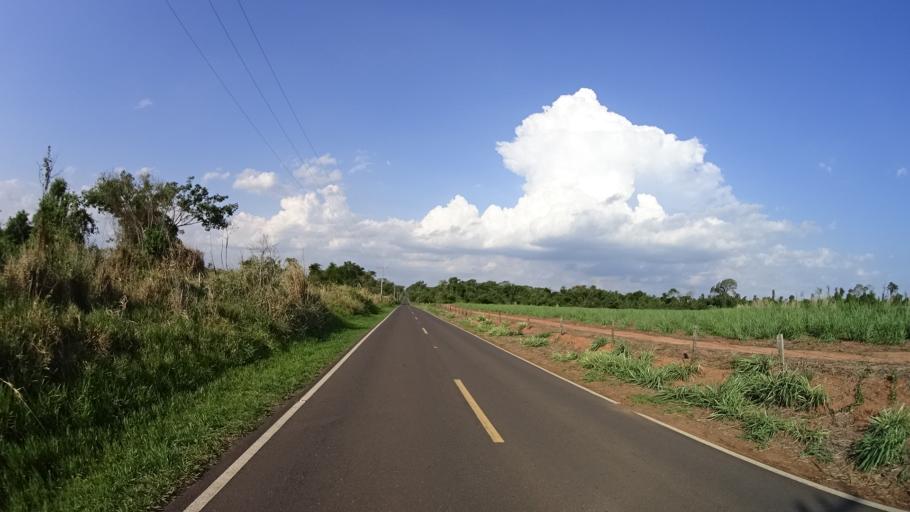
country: BR
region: Sao Paulo
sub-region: Urupes
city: Urupes
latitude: -21.3816
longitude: -49.4894
